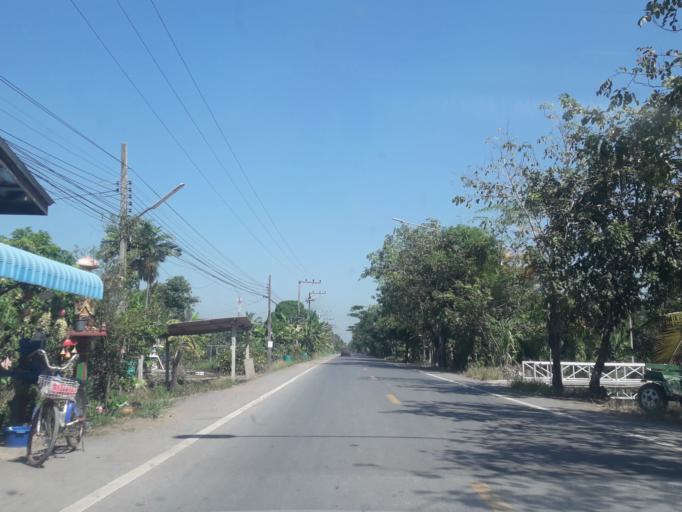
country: TH
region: Pathum Thani
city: Nong Suea
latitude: 14.1724
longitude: 100.8458
